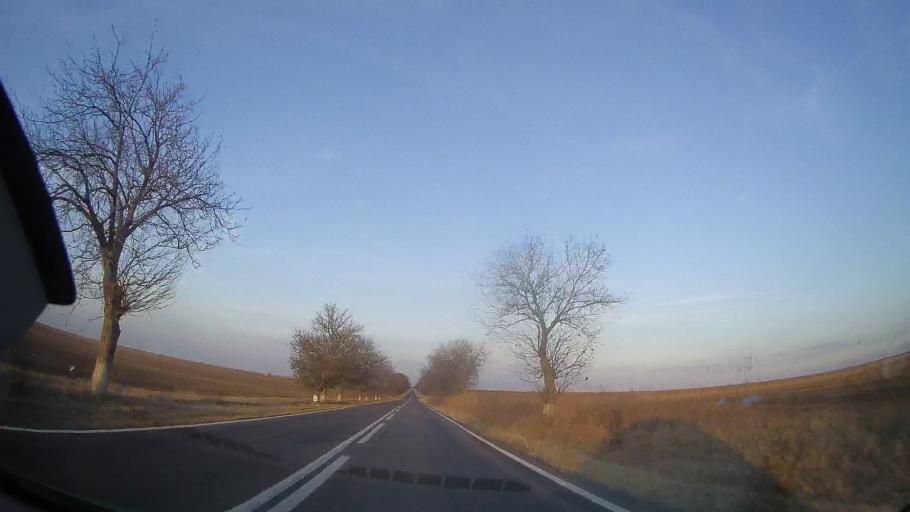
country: RO
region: Constanta
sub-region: Comuna Topraisar
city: Topraisar
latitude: 43.9874
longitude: 28.4216
